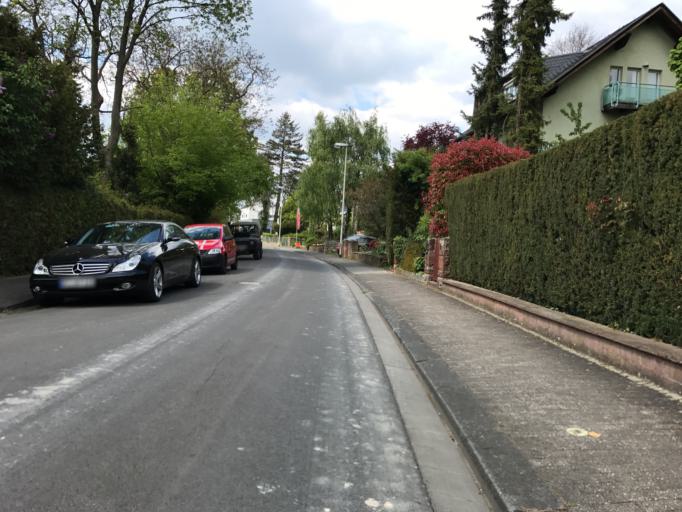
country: DE
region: Rheinland-Pfalz
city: Mainz
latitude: 49.9859
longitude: 8.2576
